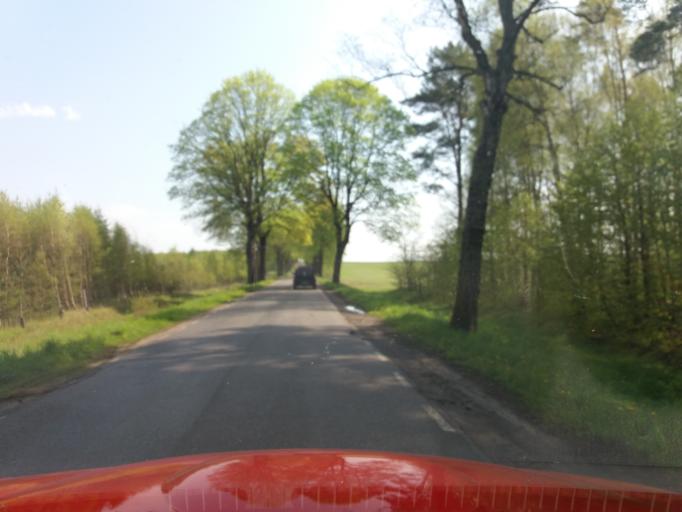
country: PL
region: West Pomeranian Voivodeship
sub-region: Powiat choszczenski
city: Drawno
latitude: 53.2490
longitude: 15.8347
